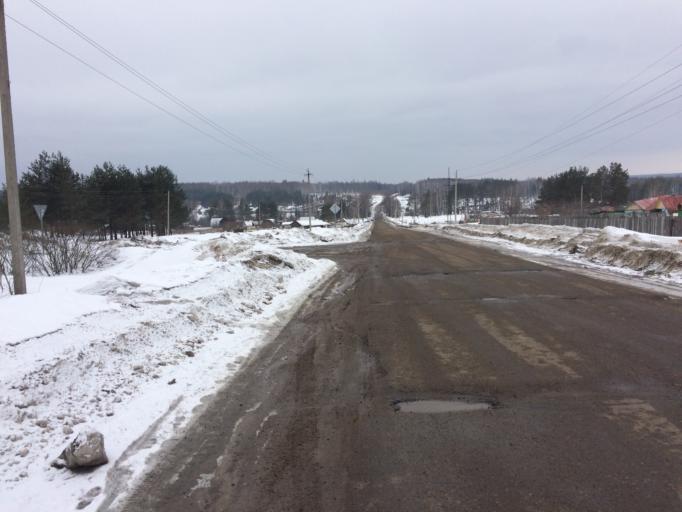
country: RU
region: Mariy-El
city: Mochalishche
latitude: 56.5456
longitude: 48.4028
